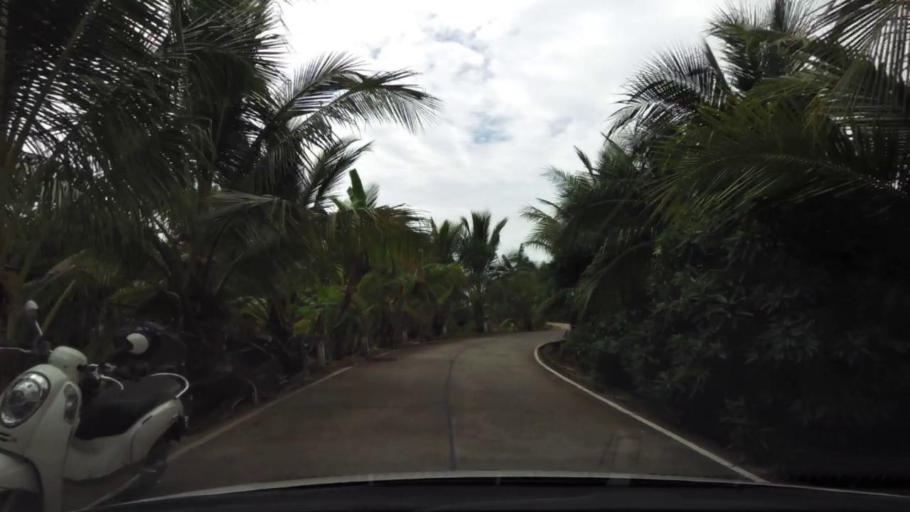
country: TH
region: Ratchaburi
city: Damnoen Saduak
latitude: 13.5493
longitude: 99.9859
